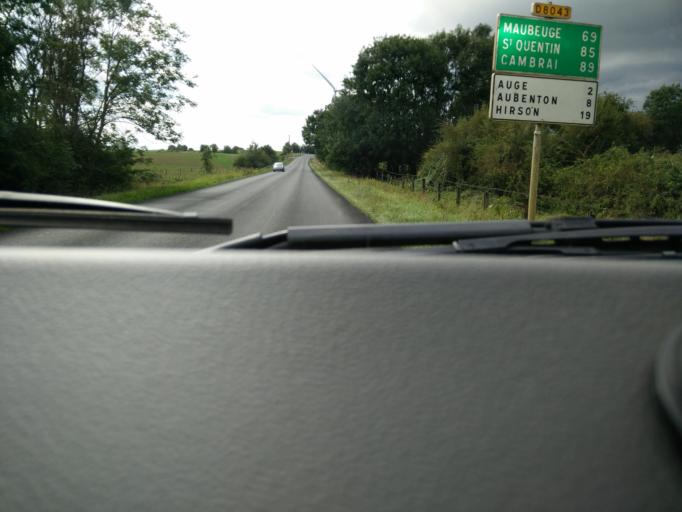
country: FR
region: Champagne-Ardenne
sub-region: Departement des Ardennes
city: Signy-le-Petit
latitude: 49.8649
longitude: 4.2973
